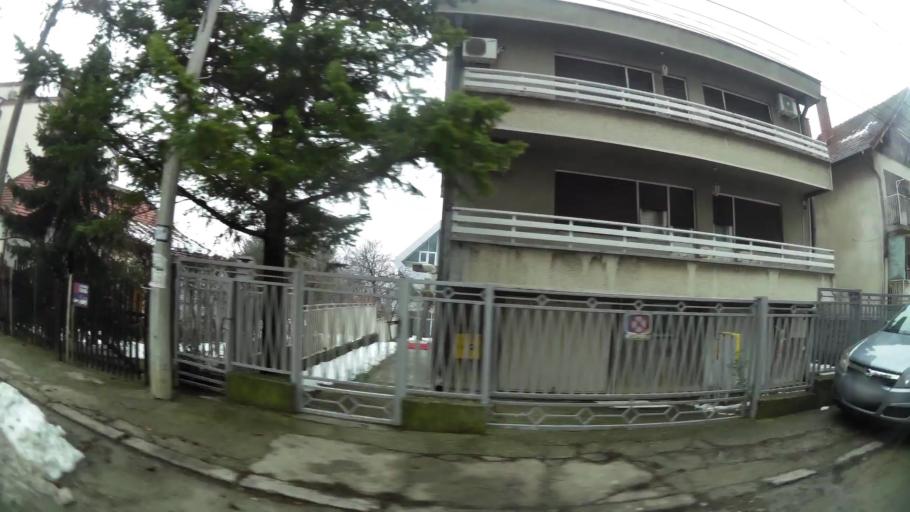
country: RS
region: Central Serbia
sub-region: Belgrade
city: Vozdovac
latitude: 44.7754
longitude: 20.4773
